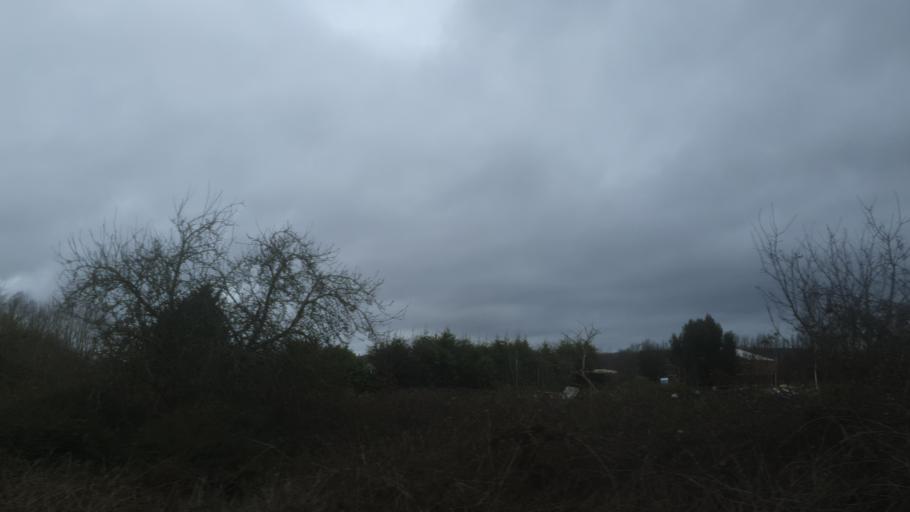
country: GB
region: England
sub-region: West Sussex
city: Pulborough
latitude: 50.9477
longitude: -0.5295
